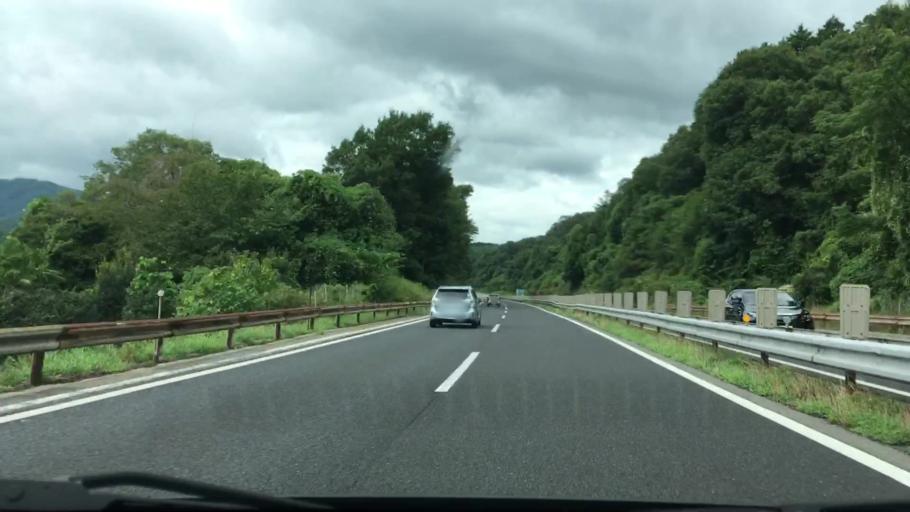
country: JP
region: Okayama
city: Tsuyama
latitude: 35.0639
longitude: 133.8854
